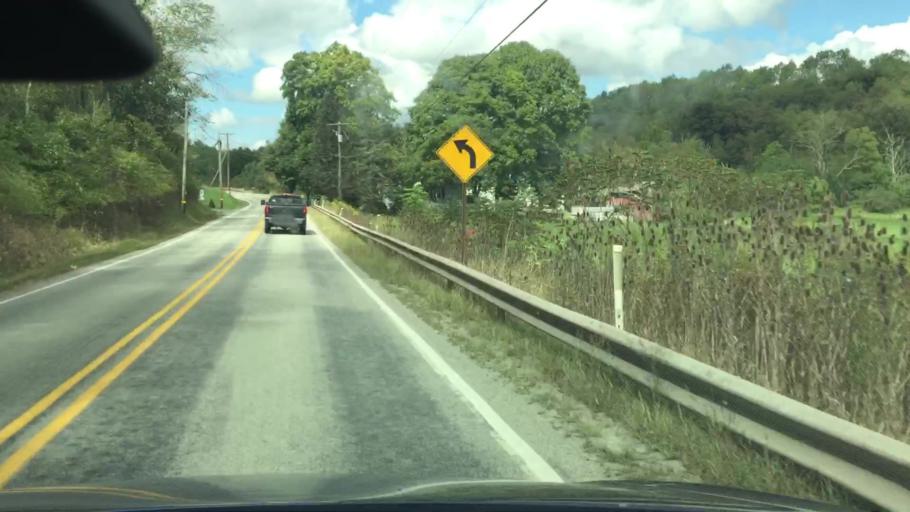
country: US
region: Pennsylvania
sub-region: Allegheny County
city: Curtisville
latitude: 40.6853
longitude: -79.8322
